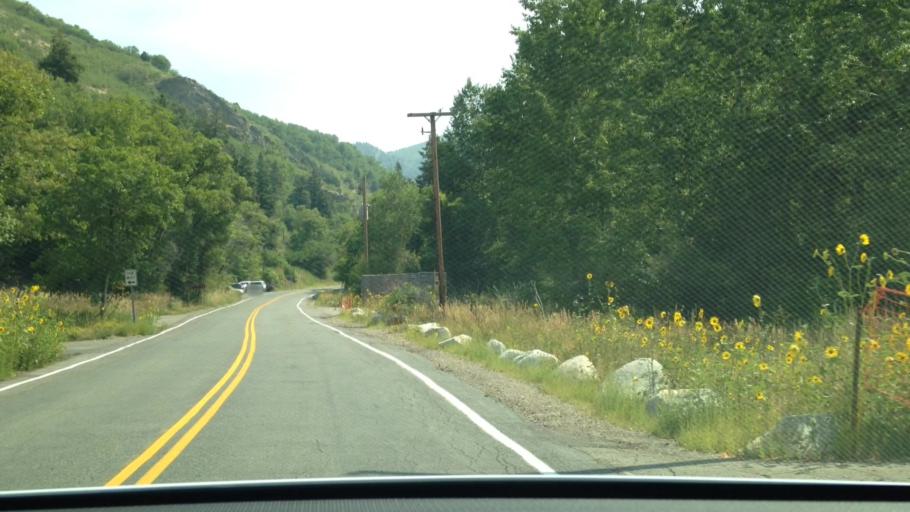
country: US
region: Utah
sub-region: Salt Lake County
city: Mount Olympus
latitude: 40.6997
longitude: -111.7181
